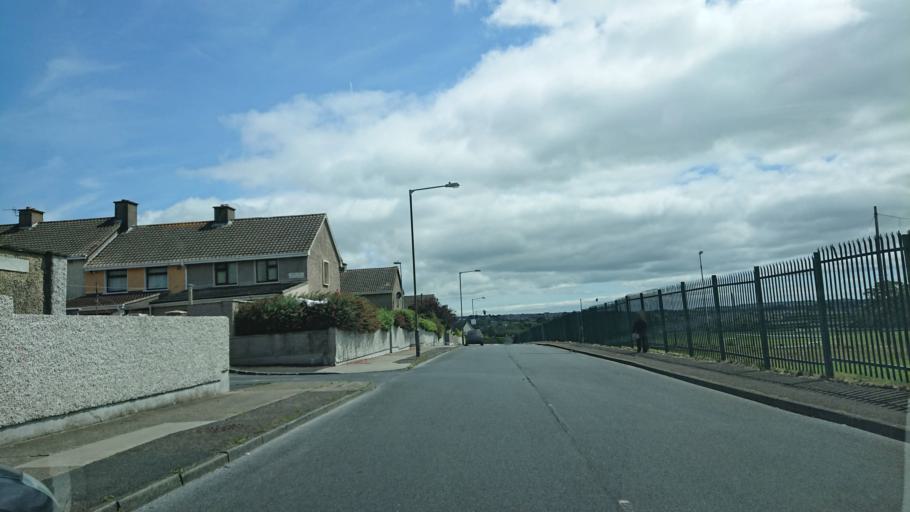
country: IE
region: Munster
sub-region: Waterford
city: Waterford
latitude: 52.2510
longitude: -7.1321
